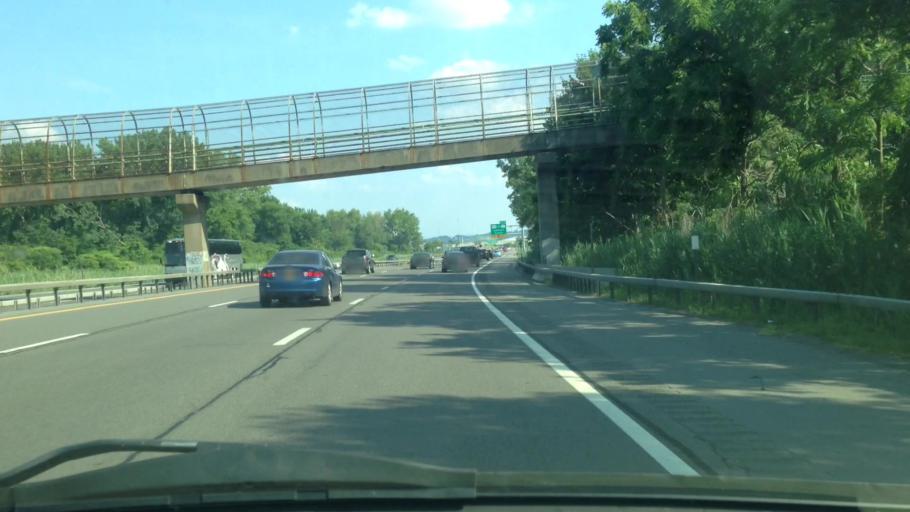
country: US
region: New York
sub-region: Onondaga County
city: Lakeland
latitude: 43.0929
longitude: -76.2348
